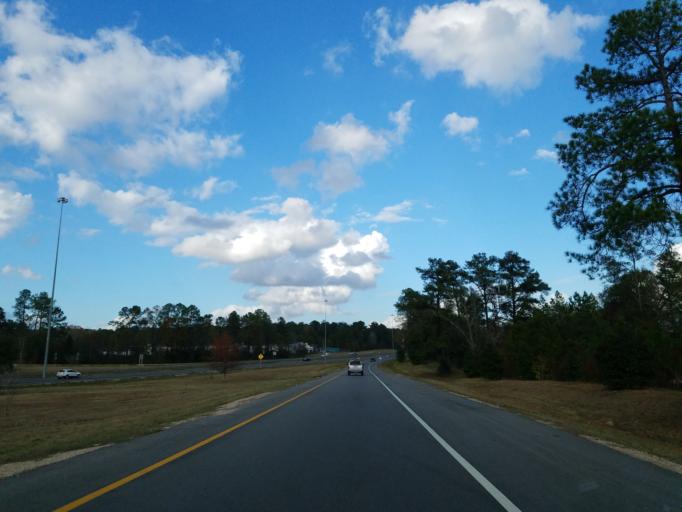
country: US
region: Mississippi
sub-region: Jones County
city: Ellisville
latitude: 31.6127
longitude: -89.2063
